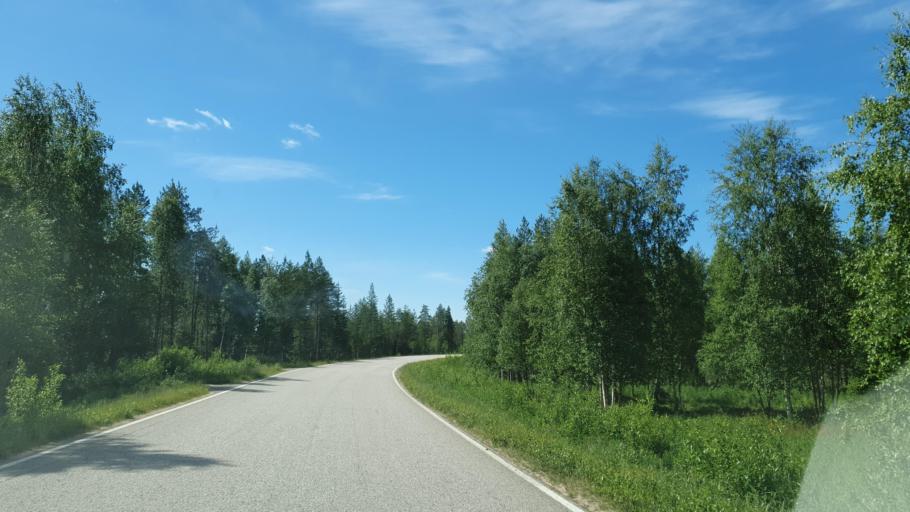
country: FI
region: Kainuu
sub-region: Kehys-Kainuu
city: Suomussalmi
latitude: 64.5753
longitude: 29.0294
